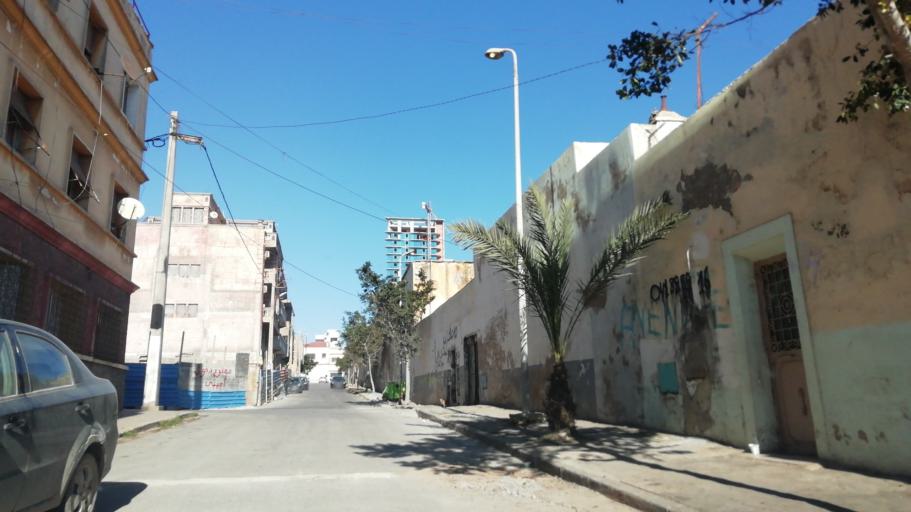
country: DZ
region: Oran
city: Oran
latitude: 35.7115
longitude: -0.6228
